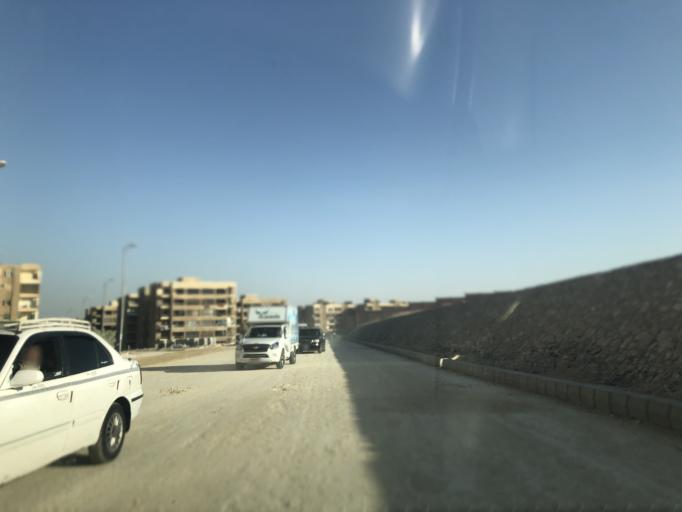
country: EG
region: Al Jizah
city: Al Jizah
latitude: 29.9880
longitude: 31.1119
